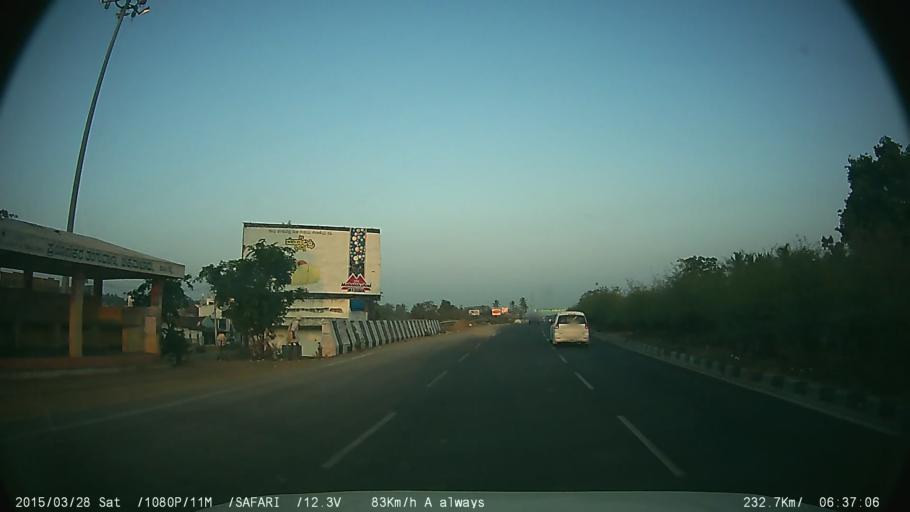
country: IN
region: Karnataka
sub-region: Ramanagara
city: Channapatna
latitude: 12.6486
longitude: 77.1870
